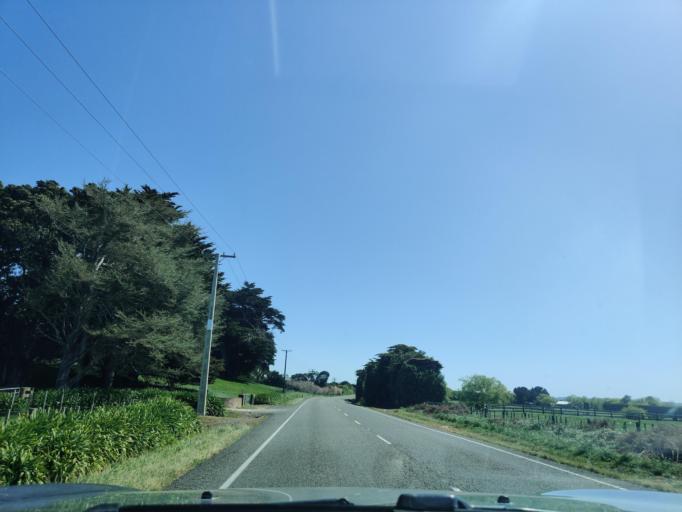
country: NZ
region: Taranaki
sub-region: South Taranaki District
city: Patea
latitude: -39.7929
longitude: 174.7042
